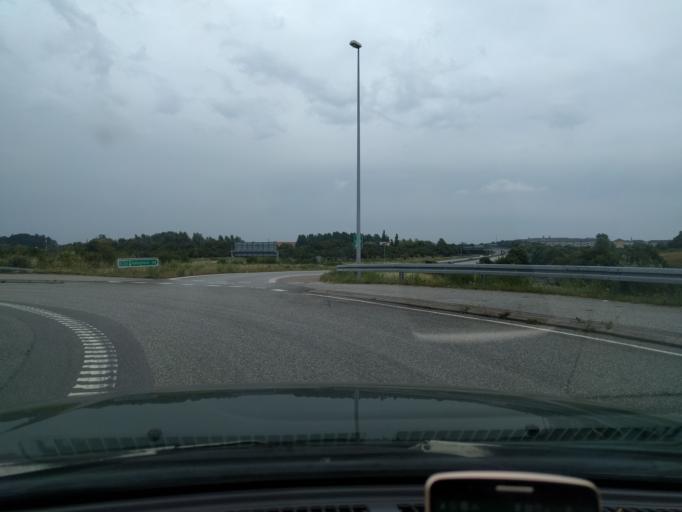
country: DK
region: Zealand
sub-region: Slagelse Kommune
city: Korsor
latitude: 55.3478
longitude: 11.1222
